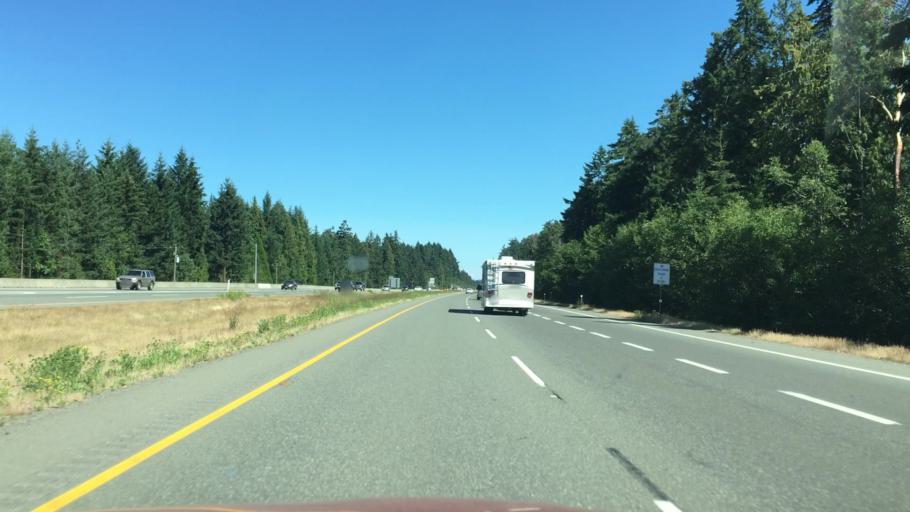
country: CA
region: British Columbia
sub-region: Regional District of Nanaimo
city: Parksville
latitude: 49.3047
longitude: -124.3181
